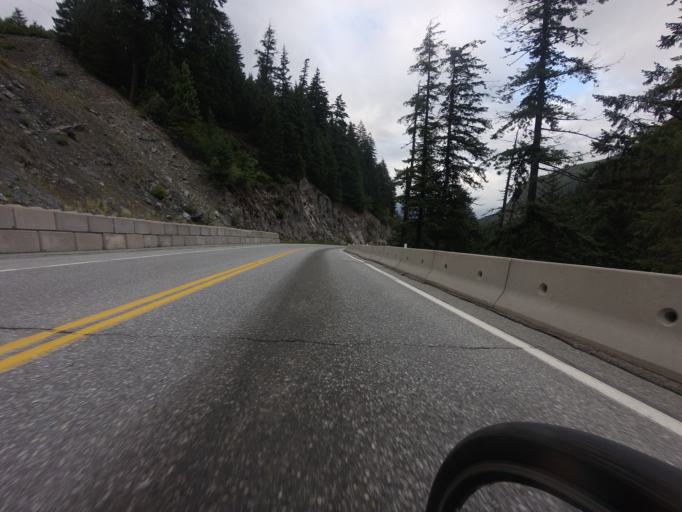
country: CA
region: British Columbia
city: Pemberton
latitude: 50.2874
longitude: -122.8415
